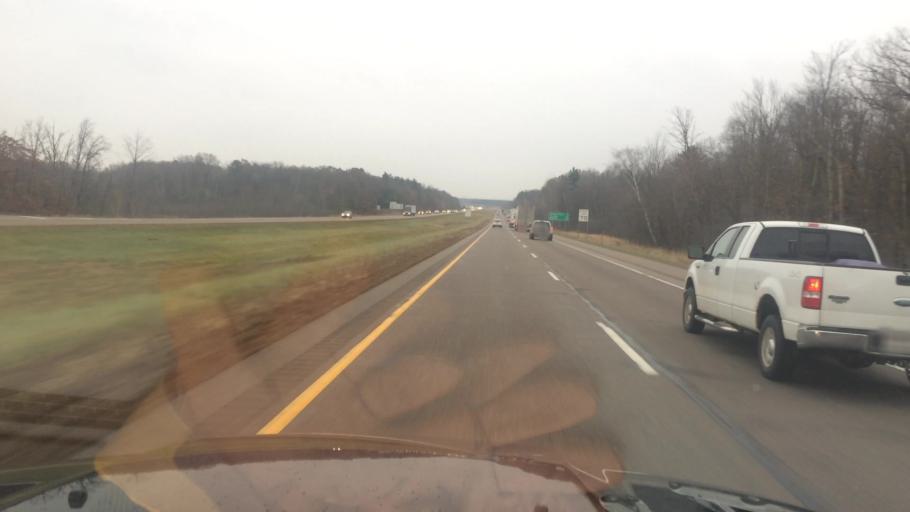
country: US
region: Wisconsin
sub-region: Portage County
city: Stevens Point
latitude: 44.5884
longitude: -89.6101
